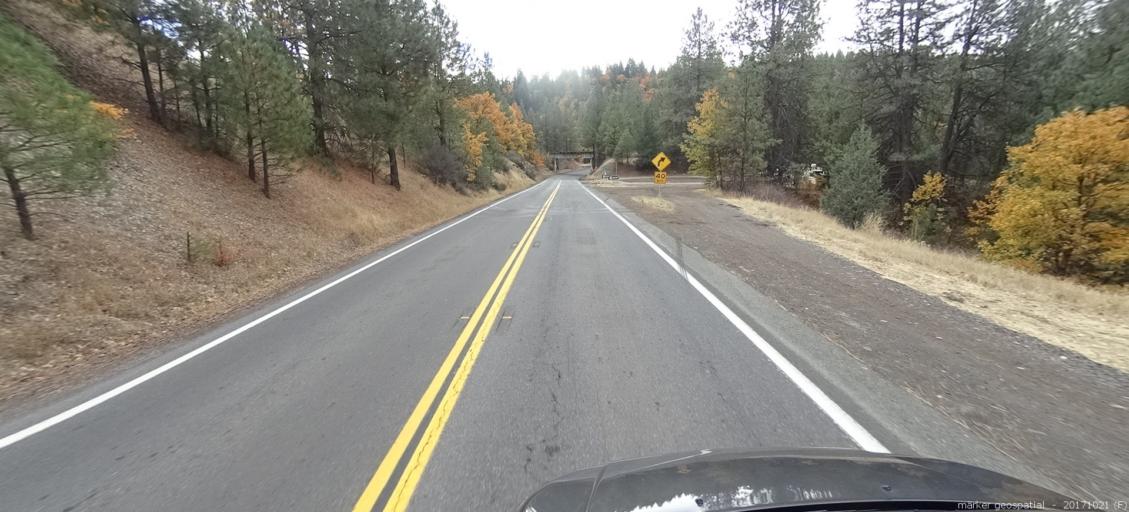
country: US
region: California
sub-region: Shasta County
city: Burney
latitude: 41.0196
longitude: -121.6214
